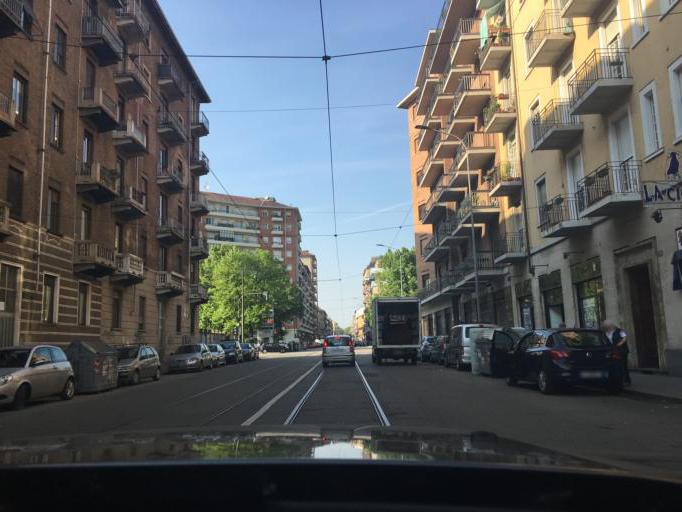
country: IT
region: Piedmont
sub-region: Provincia di Torino
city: Turin
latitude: 45.0840
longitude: 7.6929
